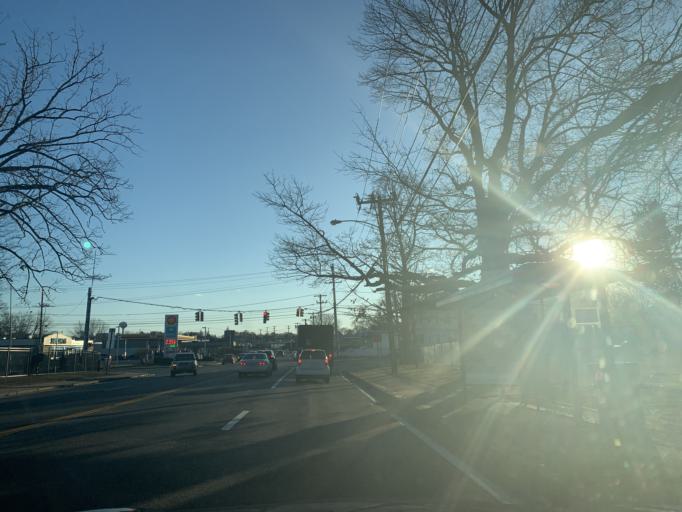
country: US
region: Rhode Island
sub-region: Providence County
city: East Providence
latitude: 41.8170
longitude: -71.3565
